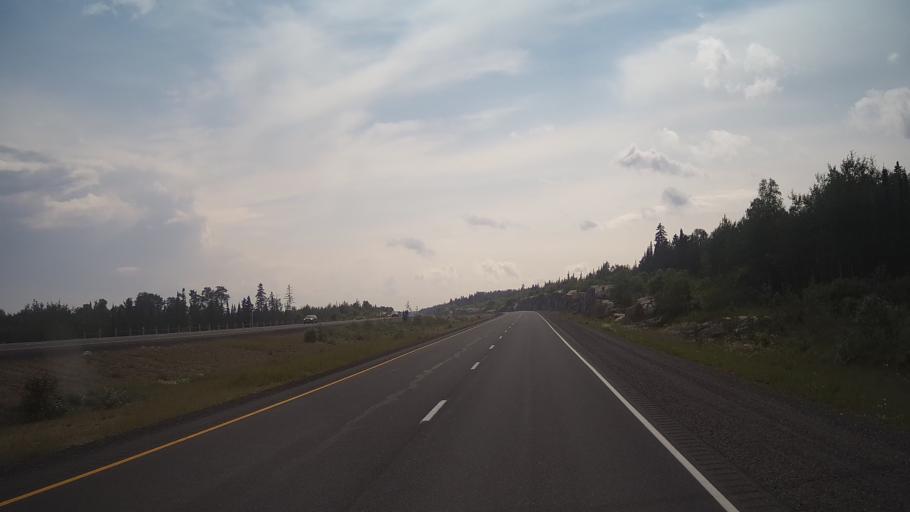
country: CA
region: Ontario
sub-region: Thunder Bay District
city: Thunder Bay
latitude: 48.5545
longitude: -88.8975
